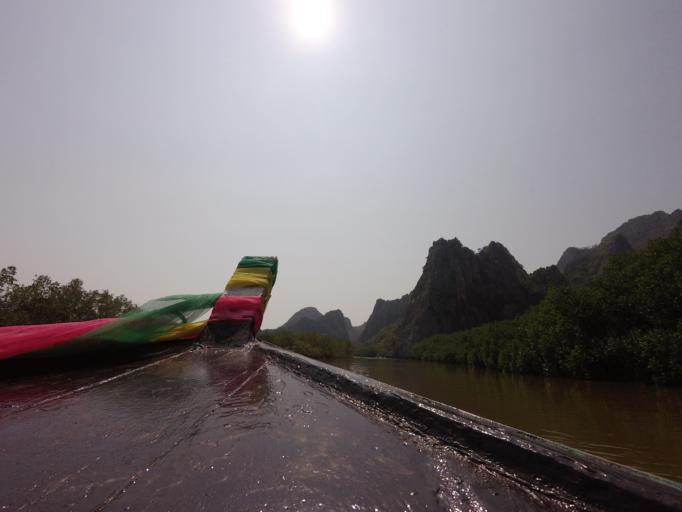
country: TH
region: Prachuap Khiri Khan
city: Kui Buri
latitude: 12.1406
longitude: 99.9574
